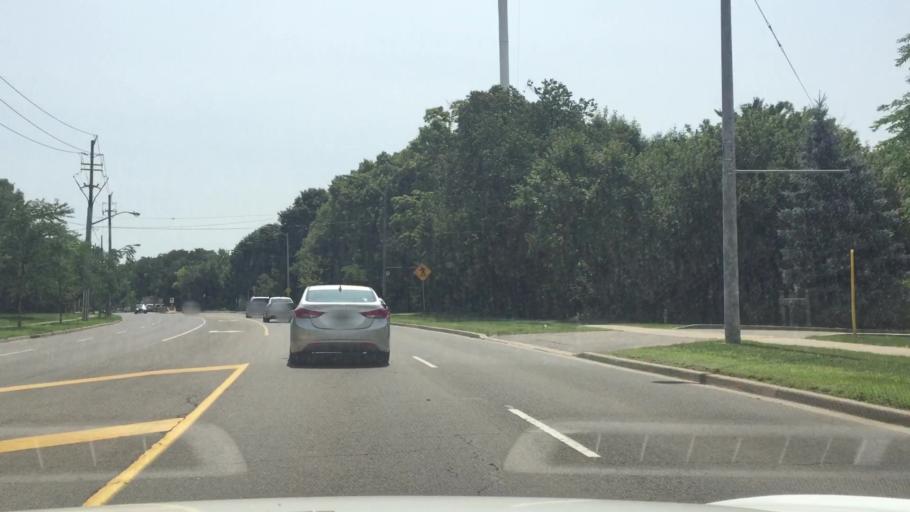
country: CA
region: Ontario
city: Willowdale
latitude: 43.7316
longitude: -79.3552
